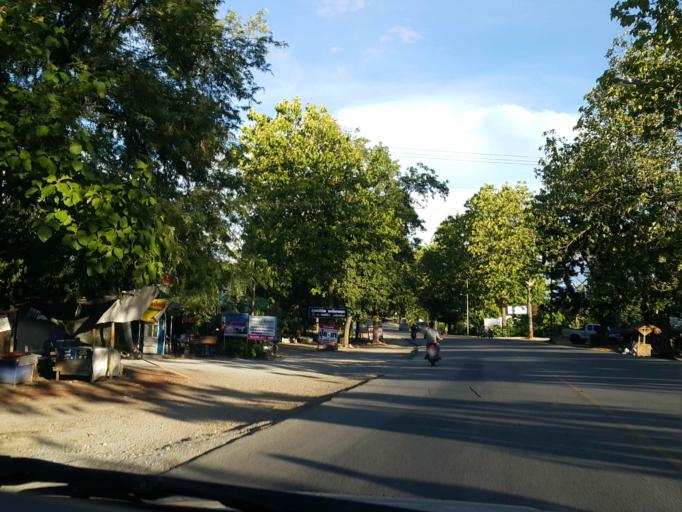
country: TH
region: Chiang Mai
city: Chom Thong
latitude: 18.4451
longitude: 98.6763
